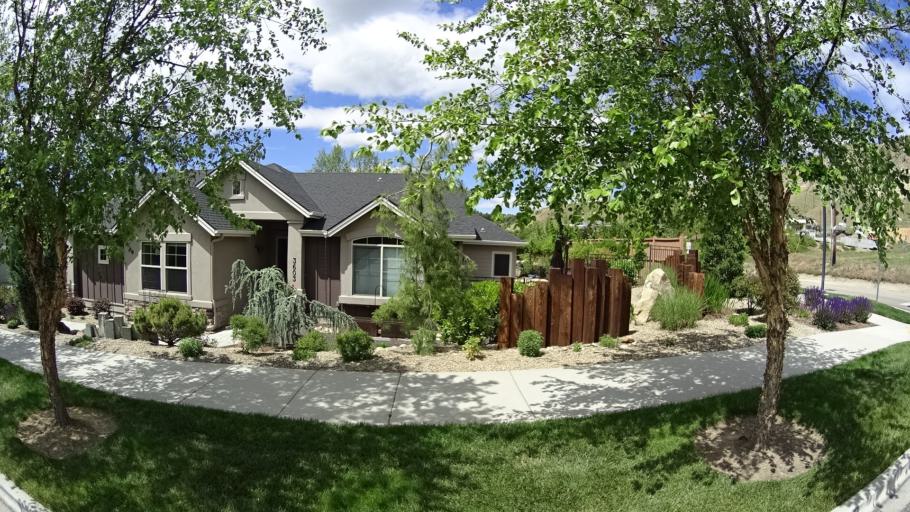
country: US
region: Idaho
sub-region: Ada County
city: Boise
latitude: 43.5800
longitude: -116.1386
